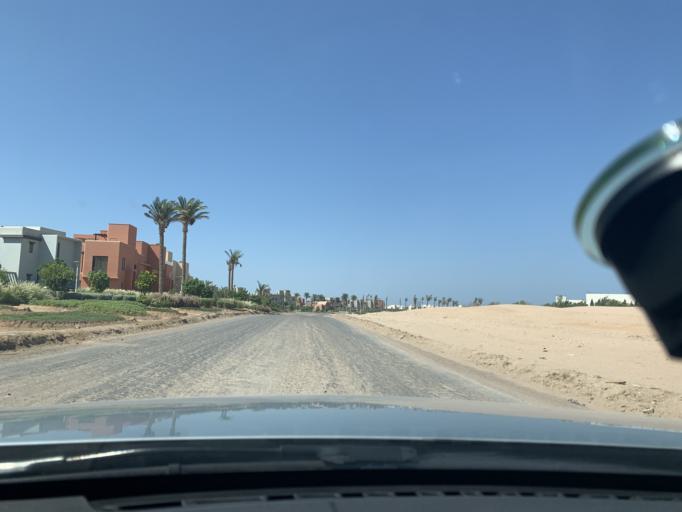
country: EG
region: Red Sea
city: El Gouna
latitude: 27.4017
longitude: 33.6640
